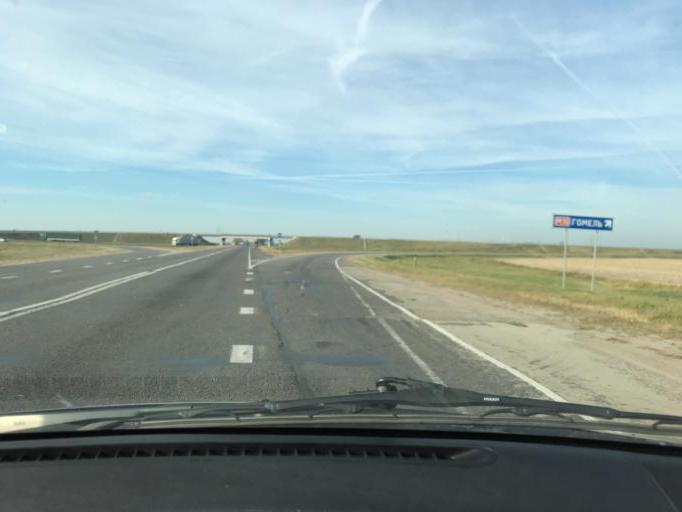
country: BY
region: Brest
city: Asnyezhytsy
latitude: 52.1812
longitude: 26.0836
